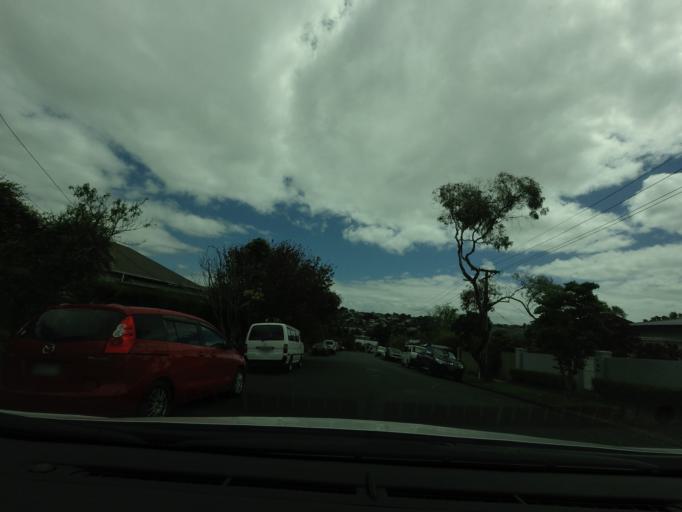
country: NZ
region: Auckland
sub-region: Auckland
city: Auckland
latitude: -36.8701
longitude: 174.7335
